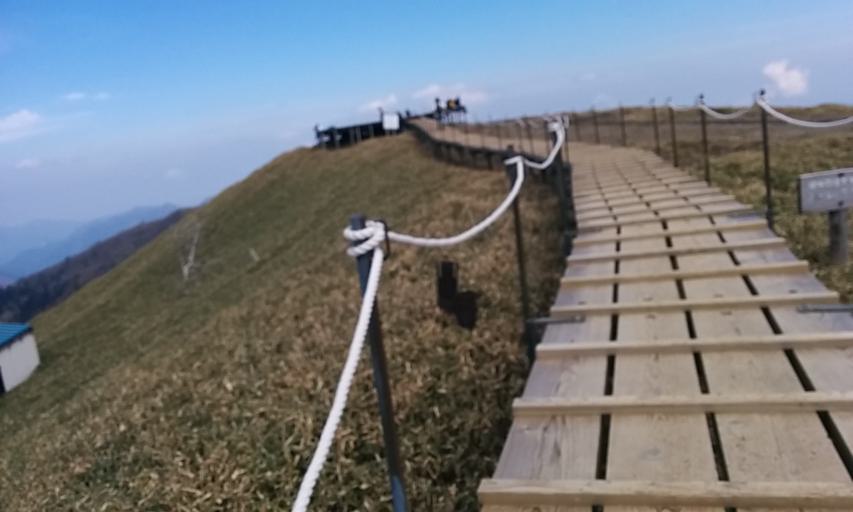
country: JP
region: Tokushima
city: Wakimachi
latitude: 33.8550
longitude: 134.0960
